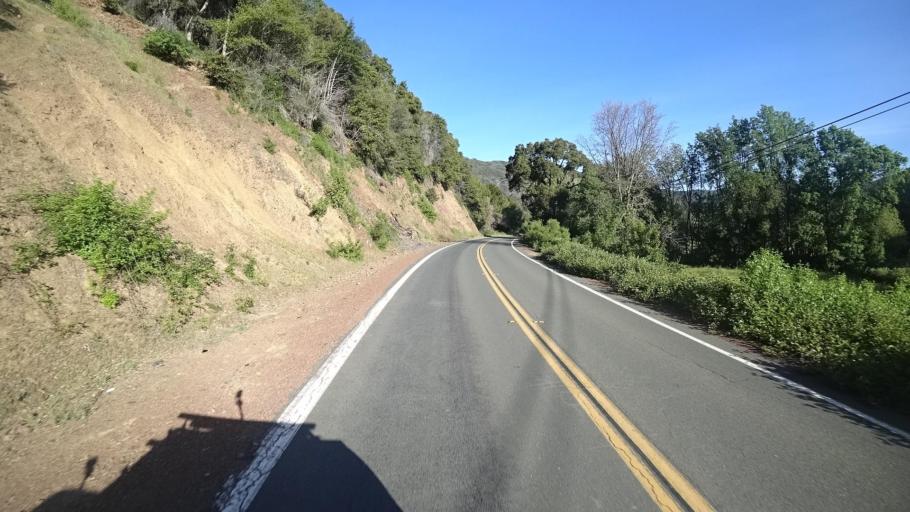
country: US
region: California
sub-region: Lake County
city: Upper Lake
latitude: 39.1227
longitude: -122.9923
